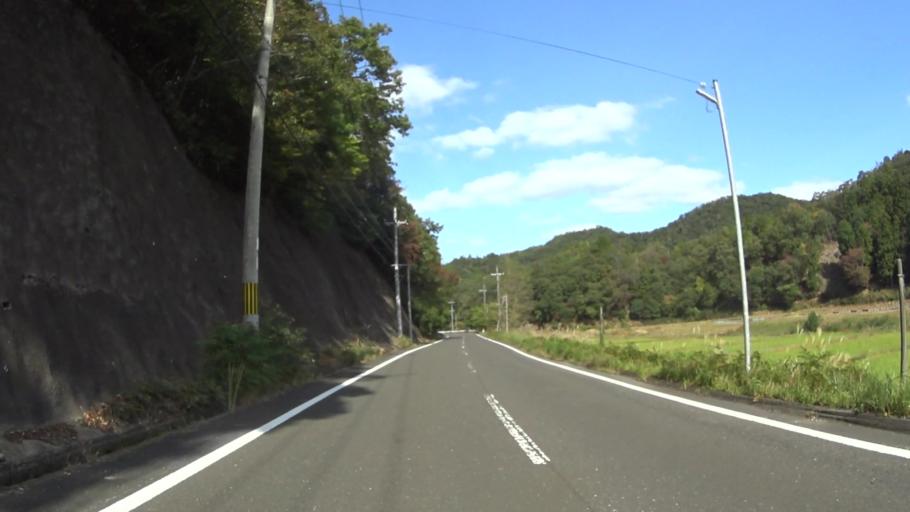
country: JP
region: Hyogo
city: Toyooka
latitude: 35.5571
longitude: 134.9789
